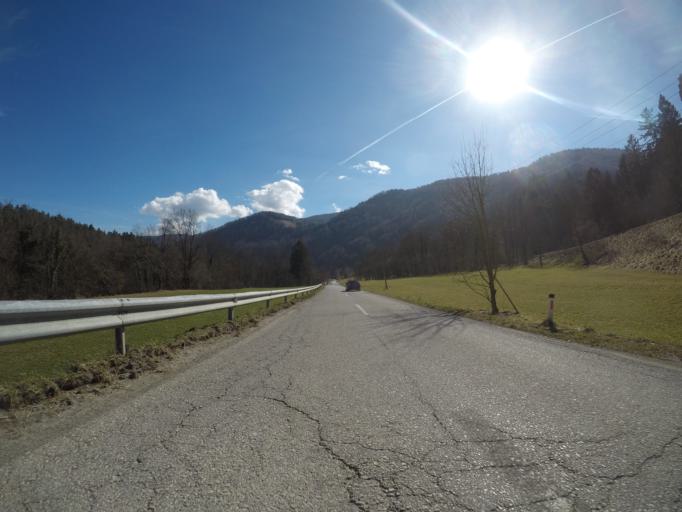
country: SI
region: Selnica ob Dravi
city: Selnica ob Dravi
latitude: 46.5390
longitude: 15.4525
